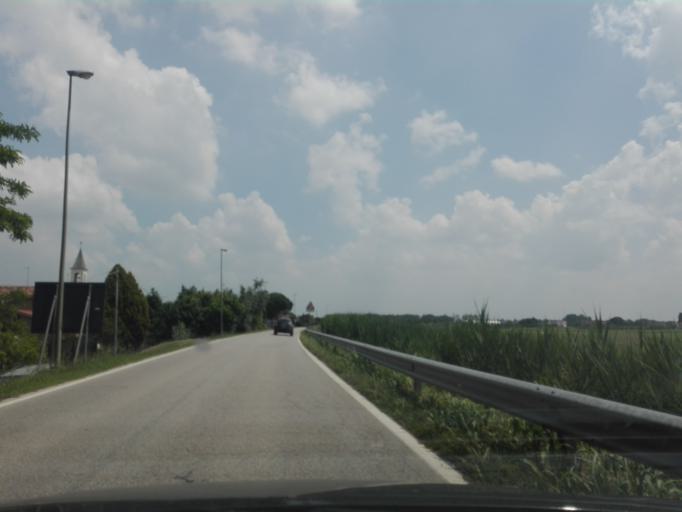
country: IT
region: Veneto
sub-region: Provincia di Rovigo
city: Adria
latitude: 45.0598
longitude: 12.0151
